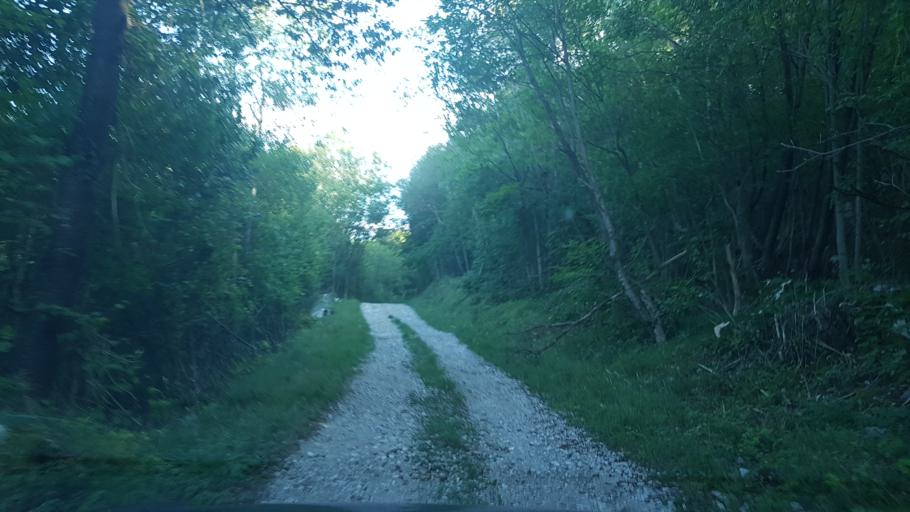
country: SI
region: Kanal
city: Deskle
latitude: 46.0212
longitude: 13.6259
